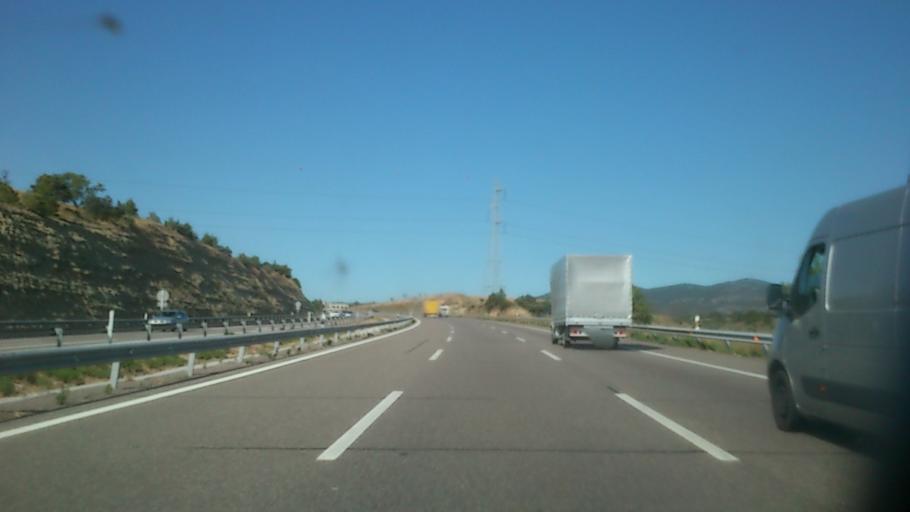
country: ES
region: Aragon
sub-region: Provincia de Zaragoza
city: Villalba de Perejil
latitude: 41.3651
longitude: -1.5832
